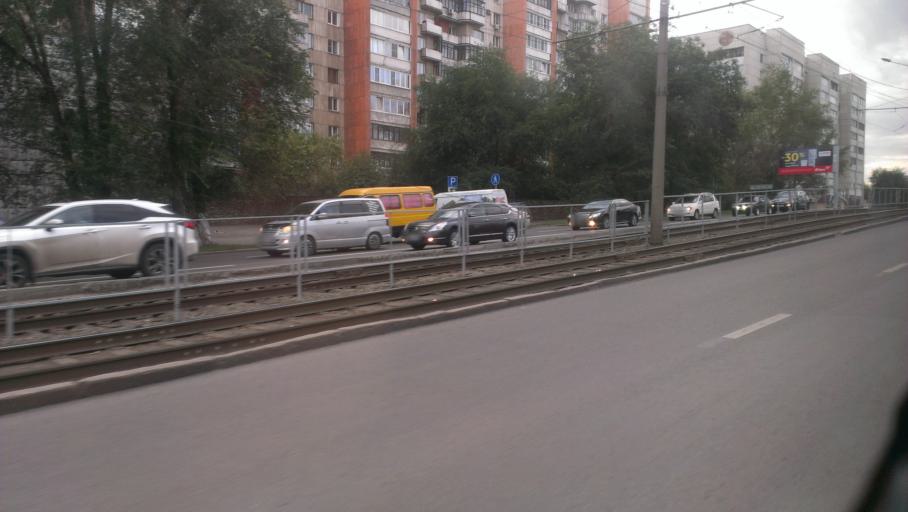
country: RU
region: Altai Krai
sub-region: Gorod Barnaulskiy
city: Barnaul
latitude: 53.3432
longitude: 83.7684
